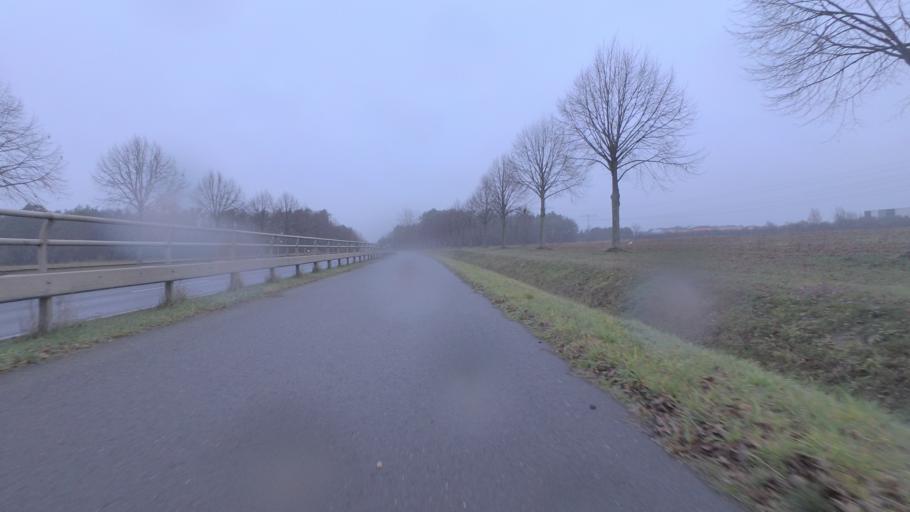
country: DE
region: Brandenburg
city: Ludwigsfelde
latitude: 52.3161
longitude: 13.2835
